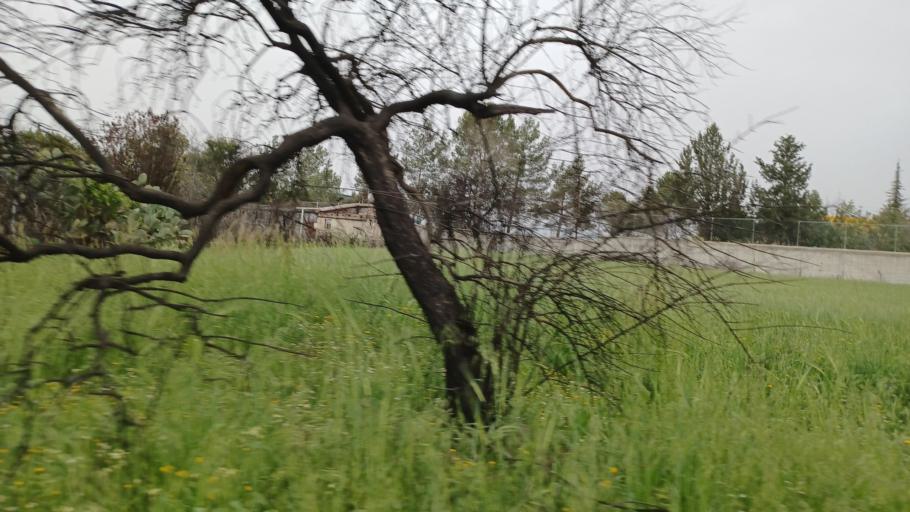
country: CY
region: Limassol
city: Parekklisha
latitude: 34.8464
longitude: 33.1450
